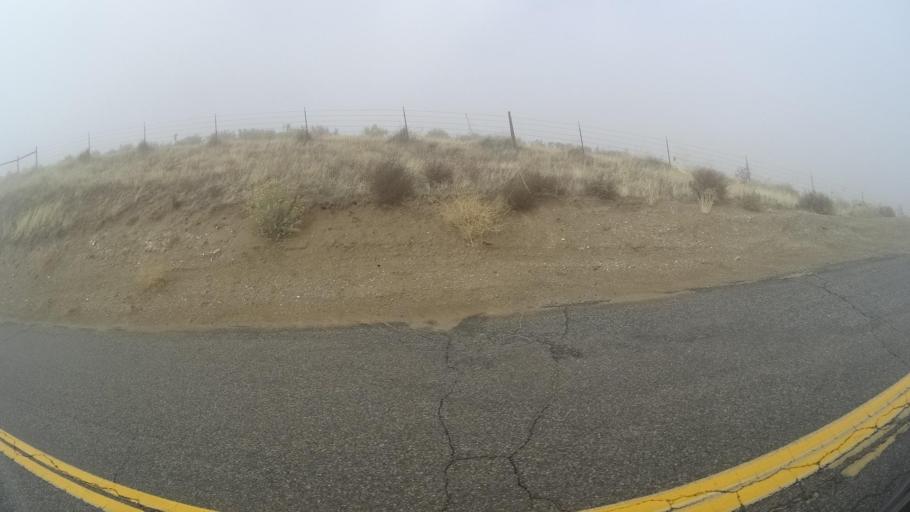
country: US
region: California
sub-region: Kern County
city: Maricopa
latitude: 34.9338
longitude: -119.4141
